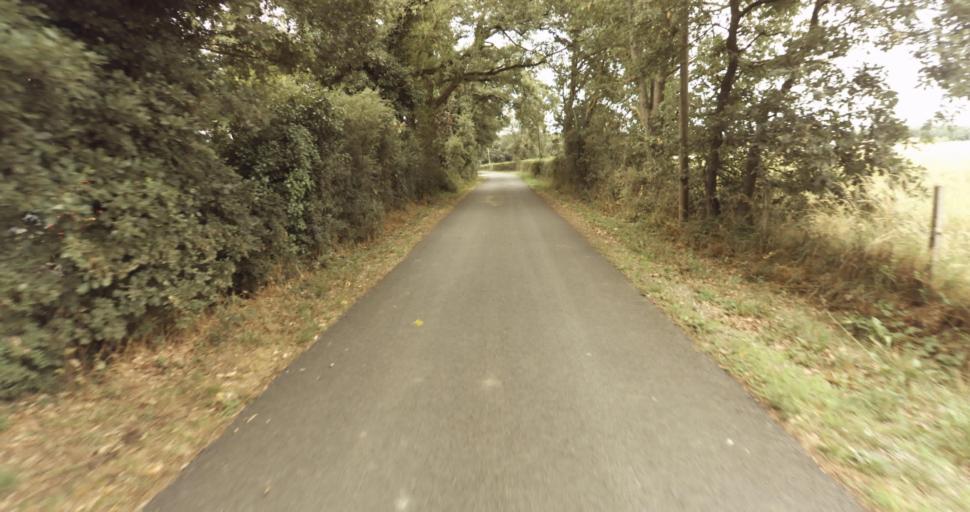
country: FR
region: Midi-Pyrenees
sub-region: Departement de la Haute-Garonne
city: Fonsorbes
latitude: 43.5570
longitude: 1.2418
